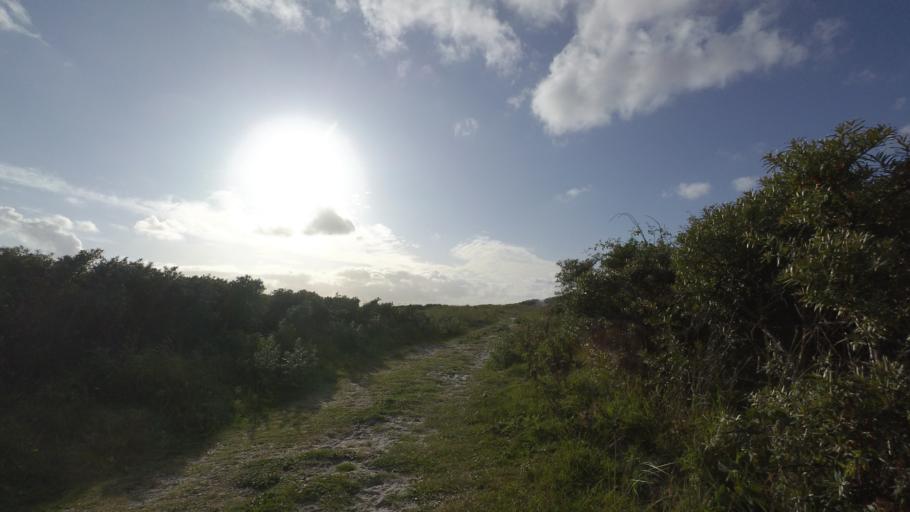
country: NL
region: Friesland
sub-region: Gemeente Dongeradeel
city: Holwerd
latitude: 53.4656
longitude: 5.9073
